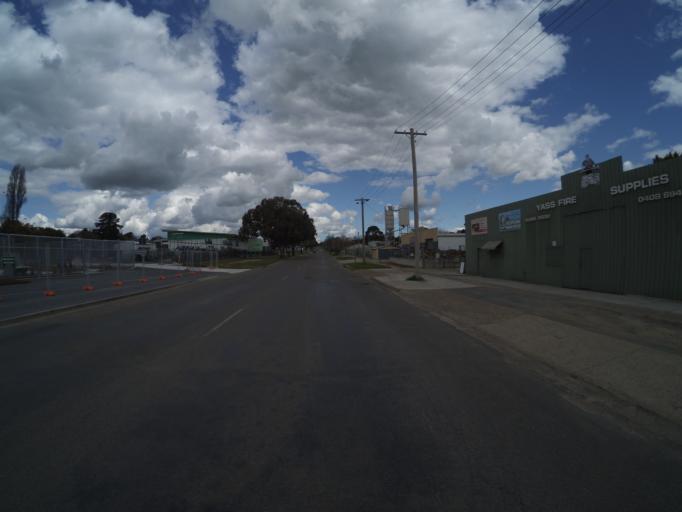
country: AU
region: New South Wales
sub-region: Yass Valley
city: Yass
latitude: -34.8495
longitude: 148.9172
